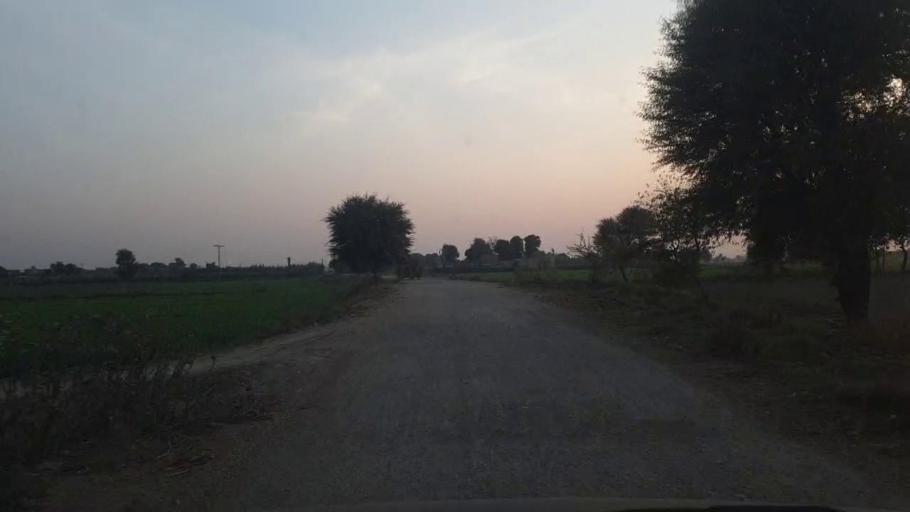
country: PK
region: Sindh
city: Bhit Shah
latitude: 25.8534
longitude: 68.5138
